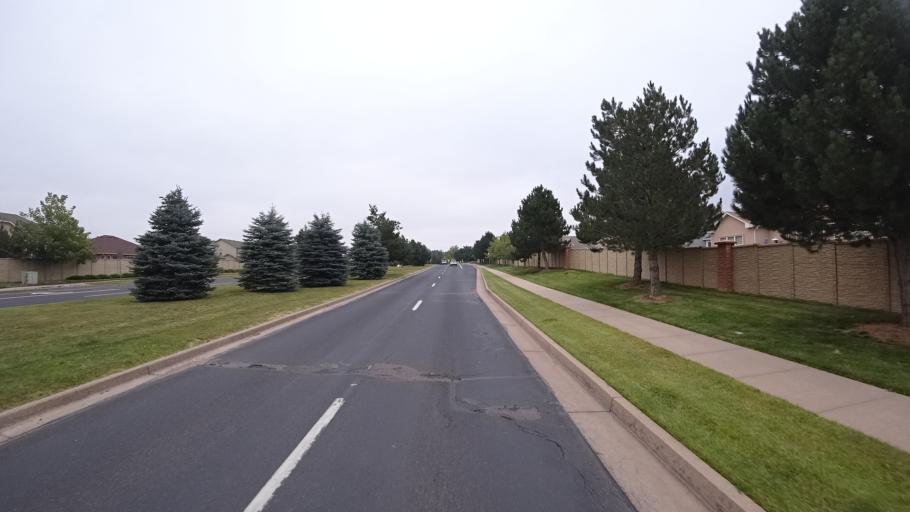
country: US
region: Colorado
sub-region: El Paso County
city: Cimarron Hills
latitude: 38.9148
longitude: -104.6939
